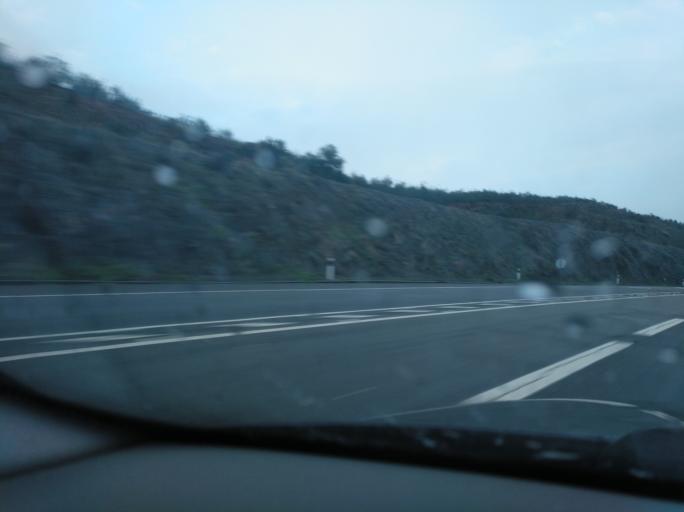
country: PT
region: Faro
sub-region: Castro Marim
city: Castro Marim
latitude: 37.3191
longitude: -7.4859
